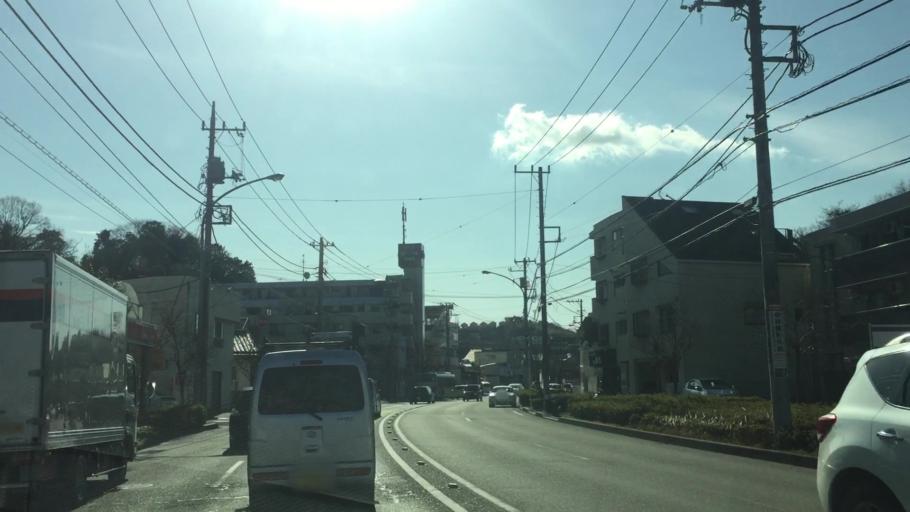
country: JP
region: Kanagawa
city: Zushi
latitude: 35.3676
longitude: 139.6135
